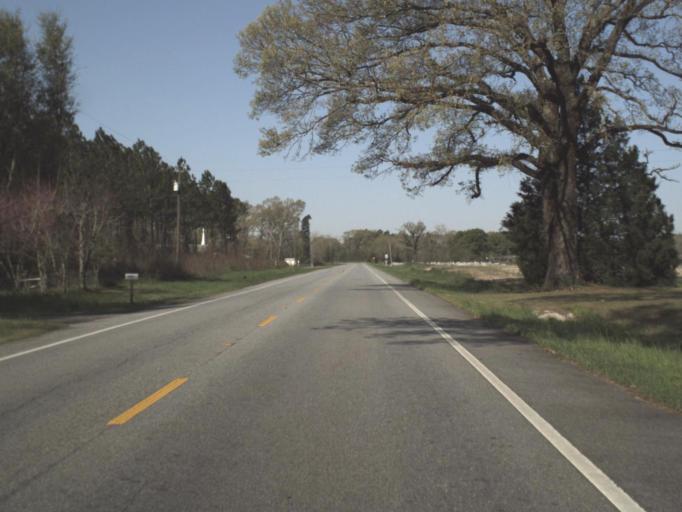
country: US
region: Florida
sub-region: Jackson County
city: Malone
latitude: 30.9753
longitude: -85.0849
